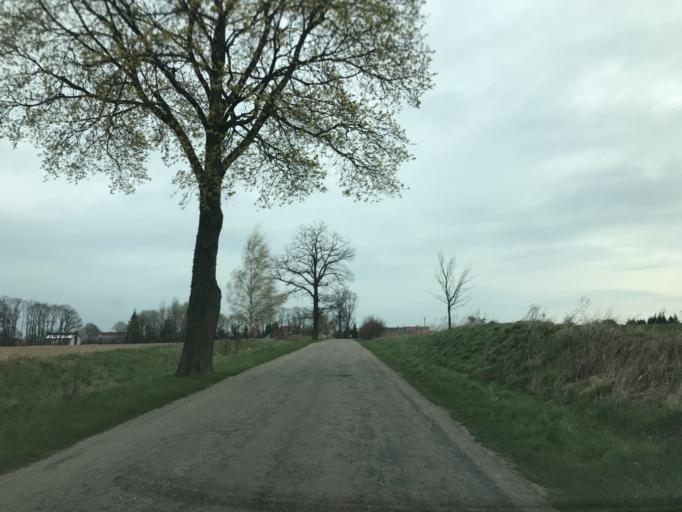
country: PL
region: Warmian-Masurian Voivodeship
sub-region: Powiat ostrodzki
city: Gierzwald
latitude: 53.6450
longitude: 20.0986
